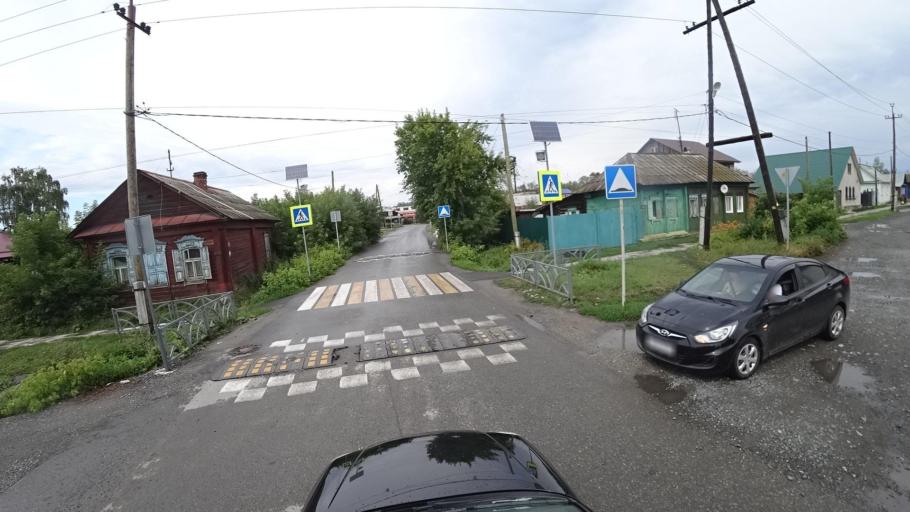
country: RU
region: Sverdlovsk
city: Kamyshlov
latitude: 56.8460
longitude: 62.7199
